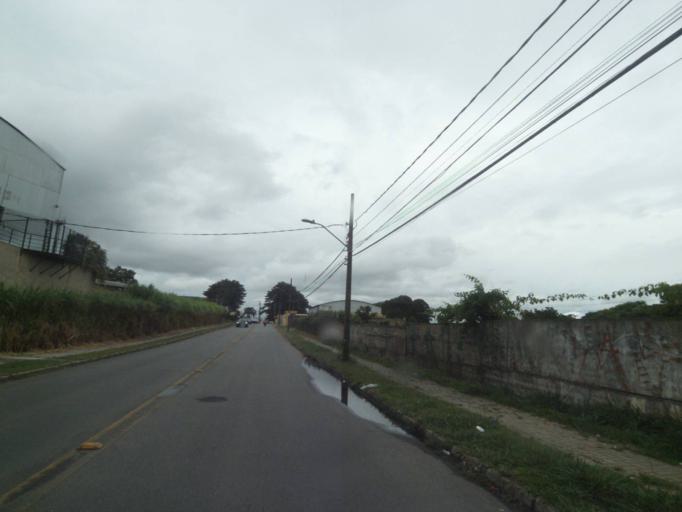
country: BR
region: Parana
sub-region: Curitiba
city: Curitiba
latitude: -25.4619
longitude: -49.3267
